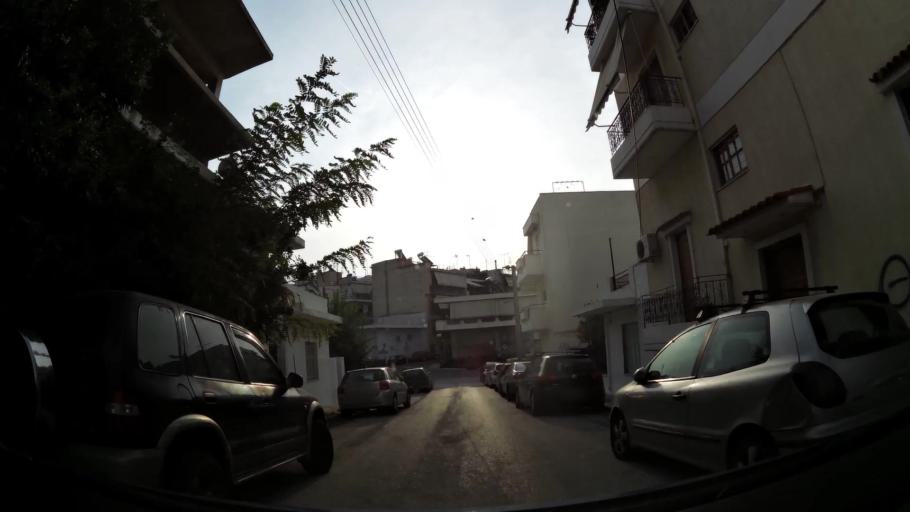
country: GR
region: Attica
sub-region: Nomarchia Athinas
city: Agios Dimitrios
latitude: 37.9395
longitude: 23.7370
